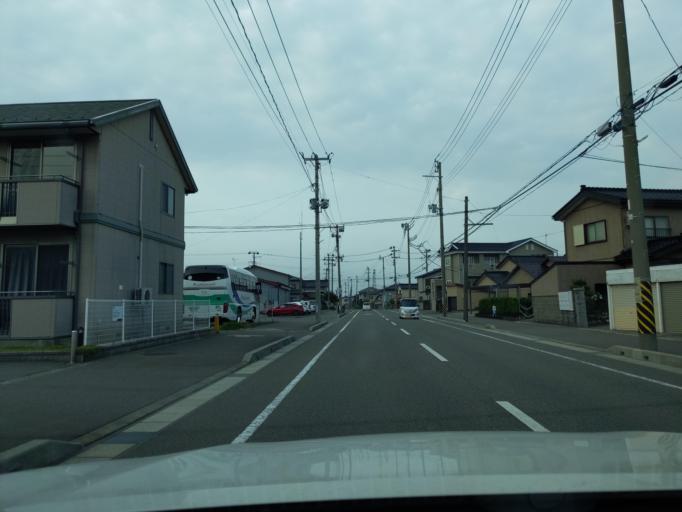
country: JP
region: Niigata
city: Kashiwazaki
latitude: 37.3796
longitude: 138.5644
